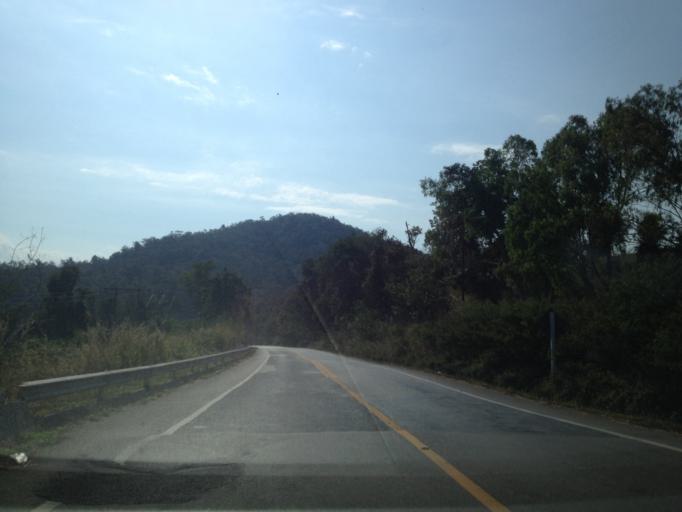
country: TH
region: Mae Hong Son
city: Pa Pae
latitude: 18.1557
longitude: 98.2344
